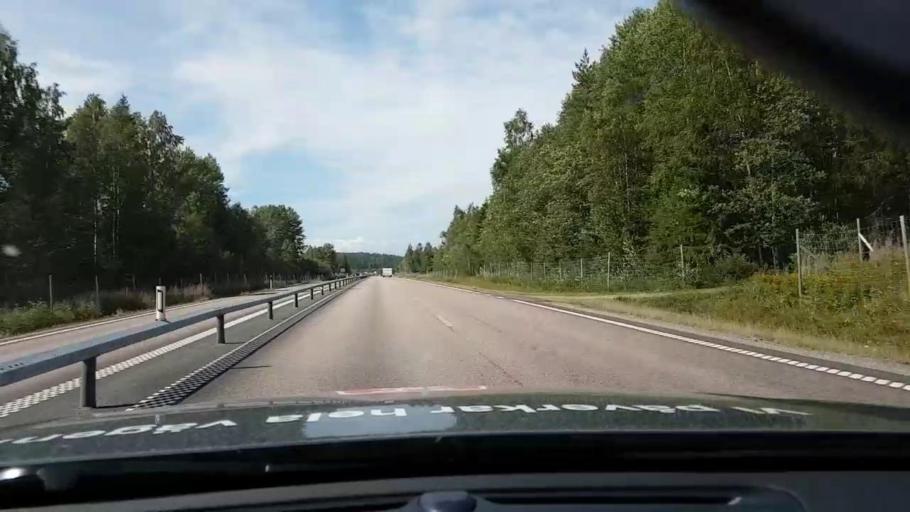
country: SE
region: Vaesternorrland
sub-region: OErnskoeldsviks Kommun
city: Ornskoldsvik
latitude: 63.3033
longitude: 18.8572
